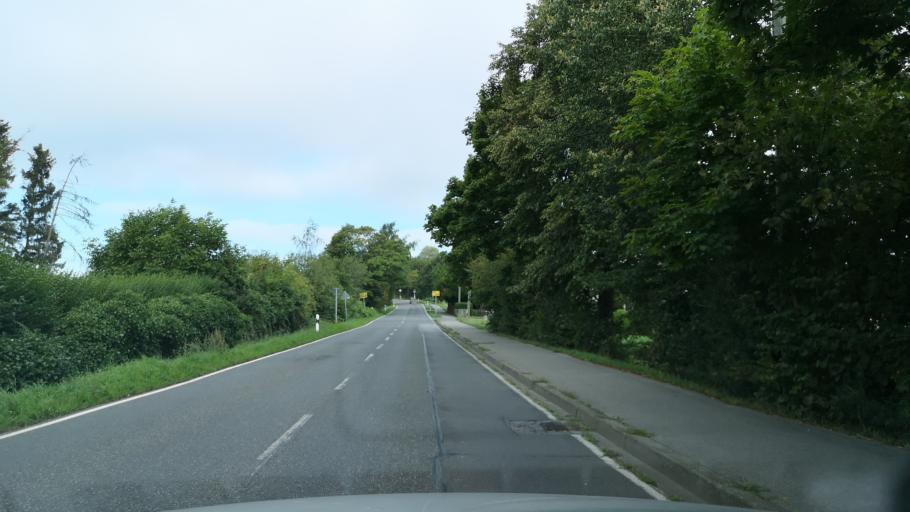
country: DE
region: North Rhine-Westphalia
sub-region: Regierungsbezirk Dusseldorf
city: Wuppertal
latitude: 51.3029
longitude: 7.1556
